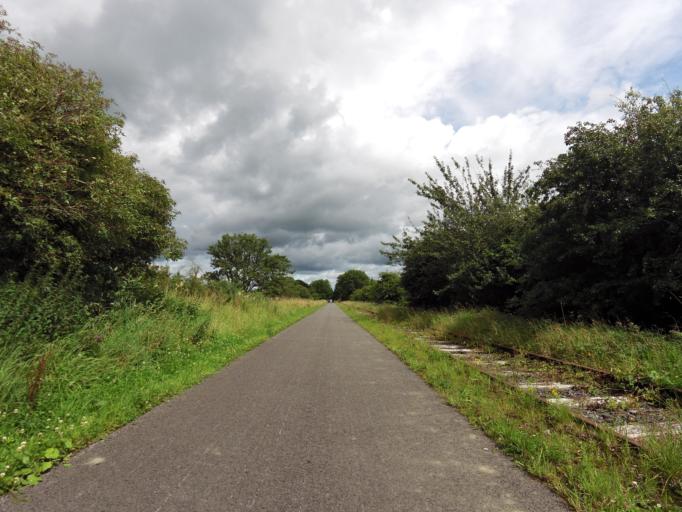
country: IE
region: Leinster
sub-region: An Iarmhi
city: An Muileann gCearr
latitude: 53.4949
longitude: -7.4462
